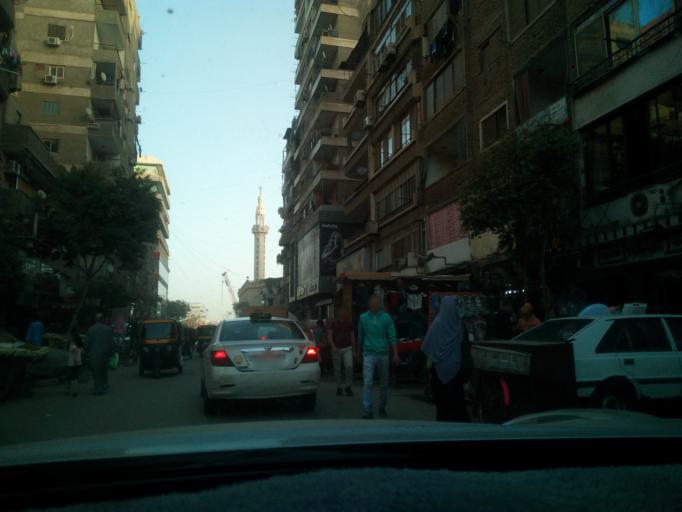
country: EG
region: Muhafazat al Qalyubiyah
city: Al Khankah
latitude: 30.1276
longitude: 31.3499
